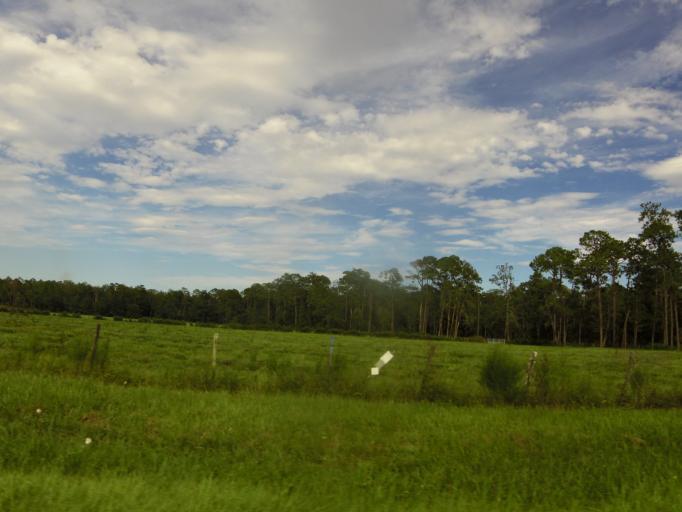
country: US
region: Florida
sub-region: Clay County
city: Green Cove Springs
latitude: 29.9429
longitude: -81.6639
